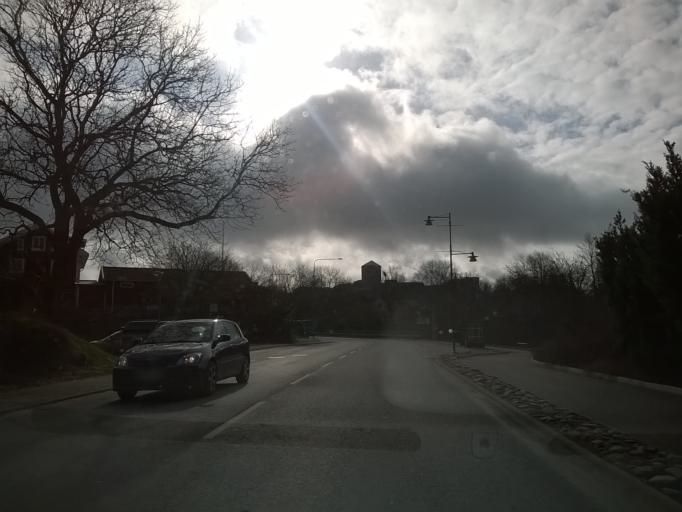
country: SE
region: Vaestra Goetaland
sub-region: Kungalvs Kommun
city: Kungalv
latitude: 57.8651
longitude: 11.9928
